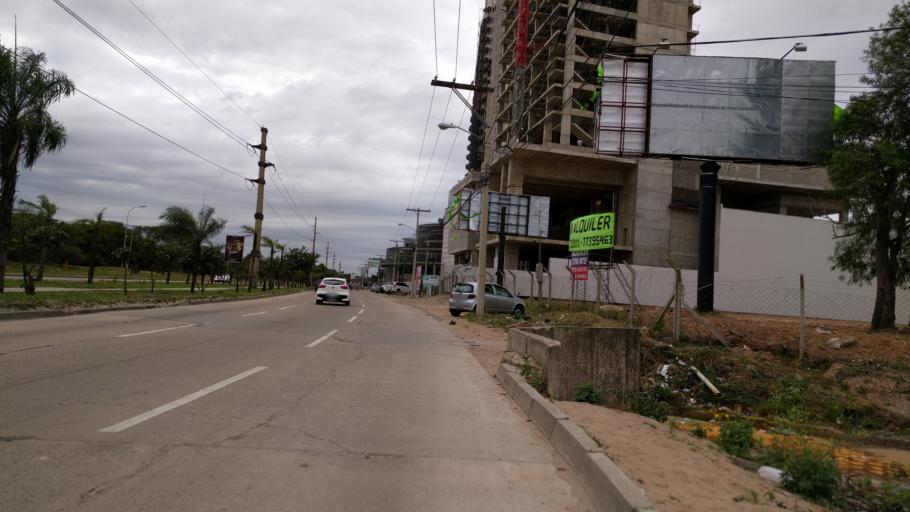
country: BO
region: Santa Cruz
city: Santa Cruz de la Sierra
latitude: -17.7620
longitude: -63.2028
